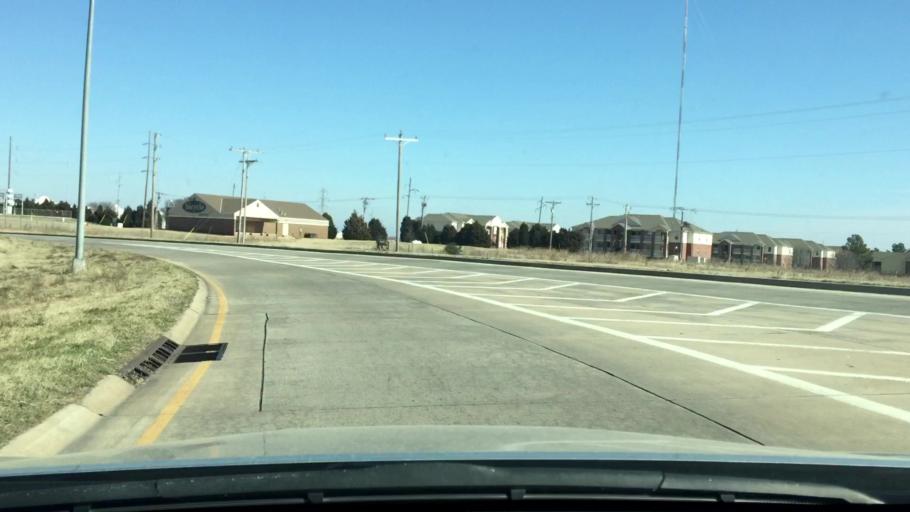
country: US
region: Oklahoma
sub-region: Oklahoma County
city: The Village
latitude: 35.5929
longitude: -97.5066
